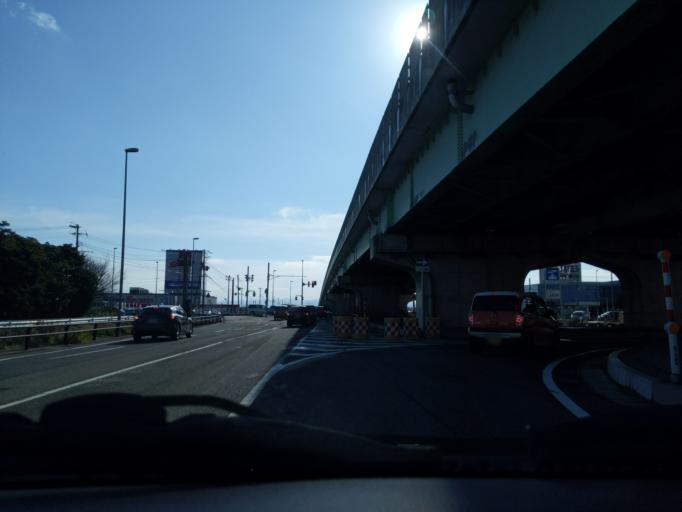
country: JP
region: Niigata
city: Kameda-honcho
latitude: 37.8704
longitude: 139.0876
